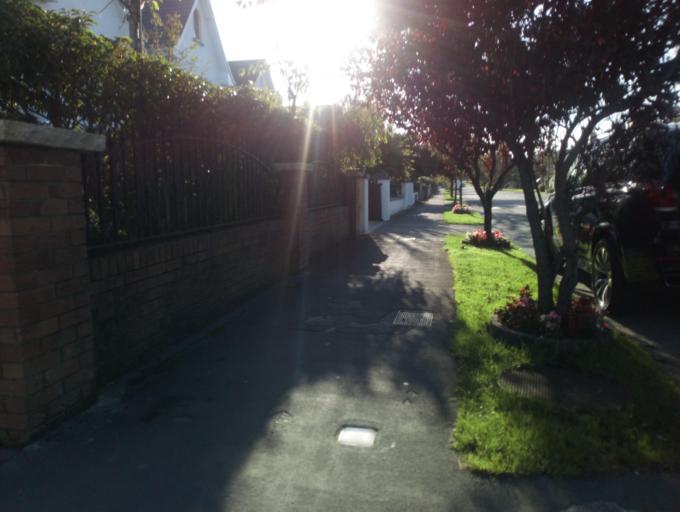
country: IE
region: Connaught
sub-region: County Galway
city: Gaillimh
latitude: 53.2644
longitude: -9.0835
